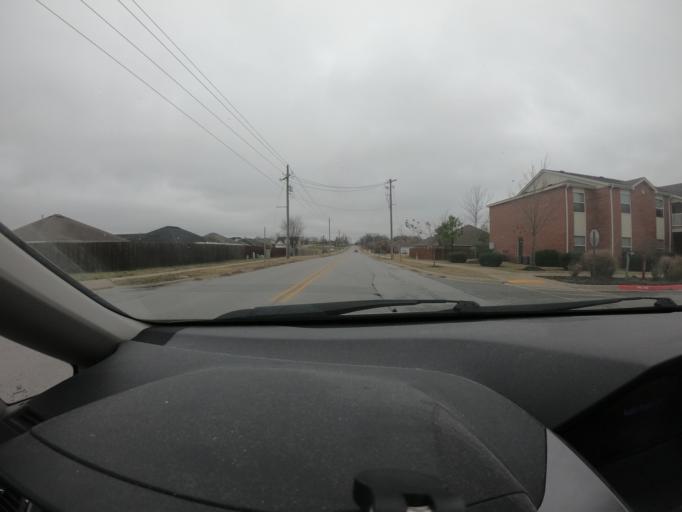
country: US
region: Arkansas
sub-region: Benton County
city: Bentonville
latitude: 36.3557
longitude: -94.2401
